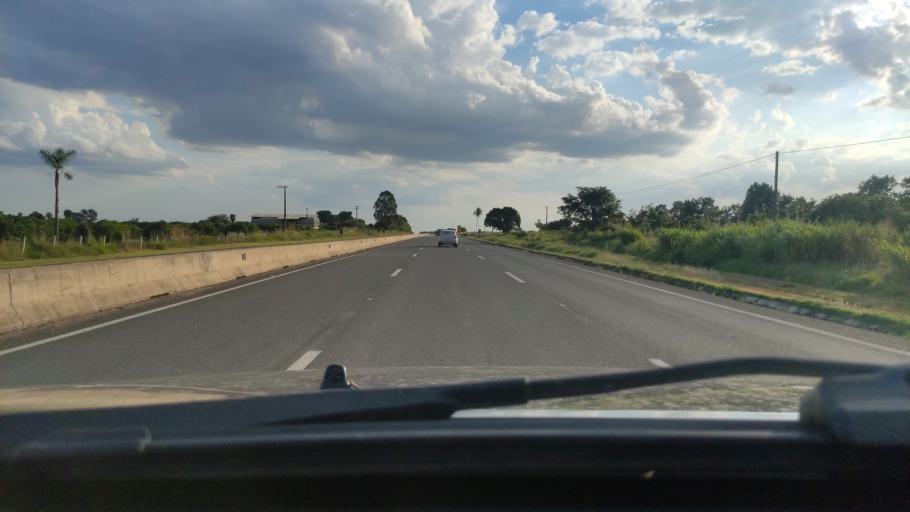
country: BR
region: Sao Paulo
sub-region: Mogi-Mirim
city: Mogi Mirim
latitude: -22.4543
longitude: -47.0906
